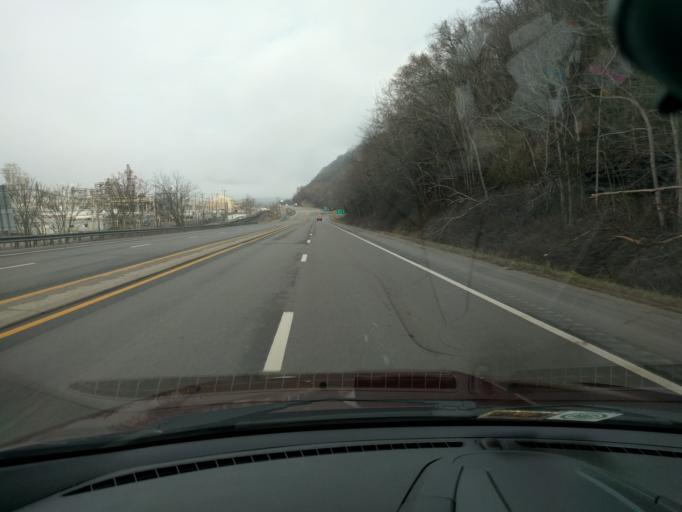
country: US
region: West Virginia
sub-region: Kanawha County
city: Belle
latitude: 38.2404
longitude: -81.5470
